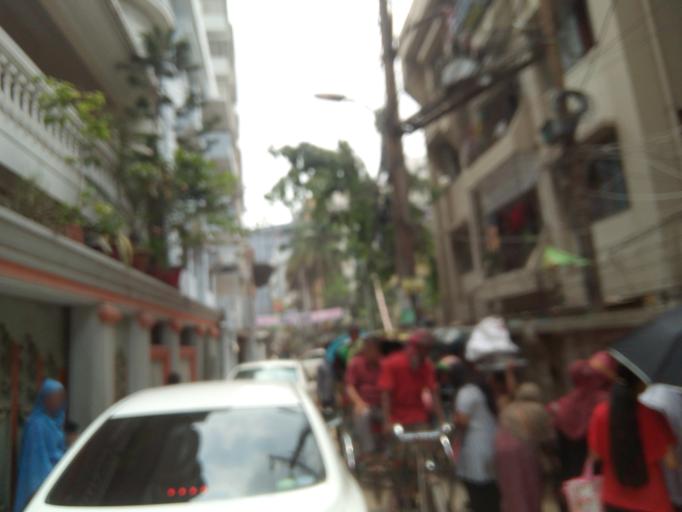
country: BD
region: Dhaka
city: Paltan
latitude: 23.7441
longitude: 90.4110
